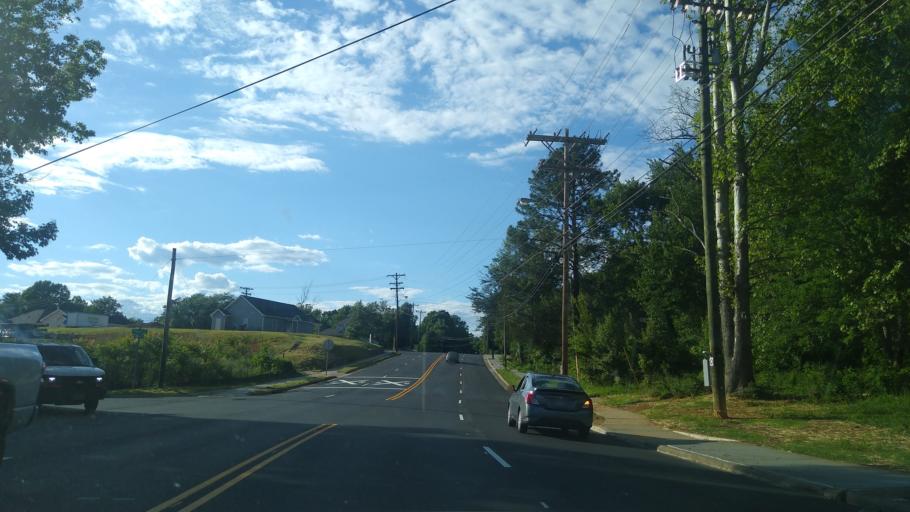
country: US
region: North Carolina
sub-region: Guilford County
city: Greensboro
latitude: 36.1263
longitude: -79.7734
